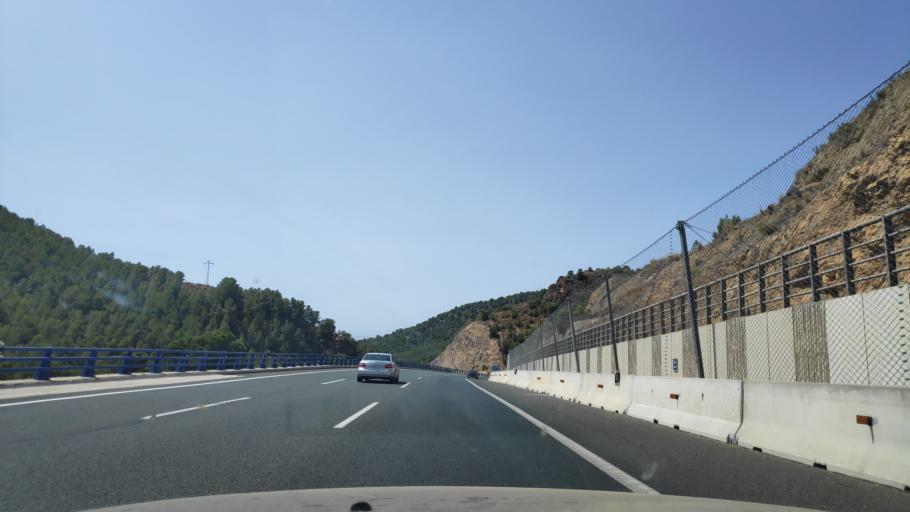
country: ES
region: Murcia
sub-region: Murcia
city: Murcia
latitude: 37.9029
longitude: -1.1442
